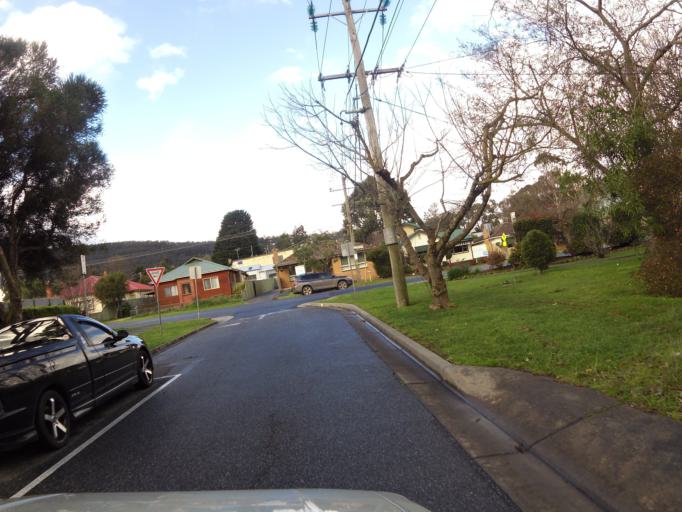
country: AU
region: Victoria
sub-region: Knox
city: Ferntree Gully
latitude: -37.8949
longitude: 145.3090
